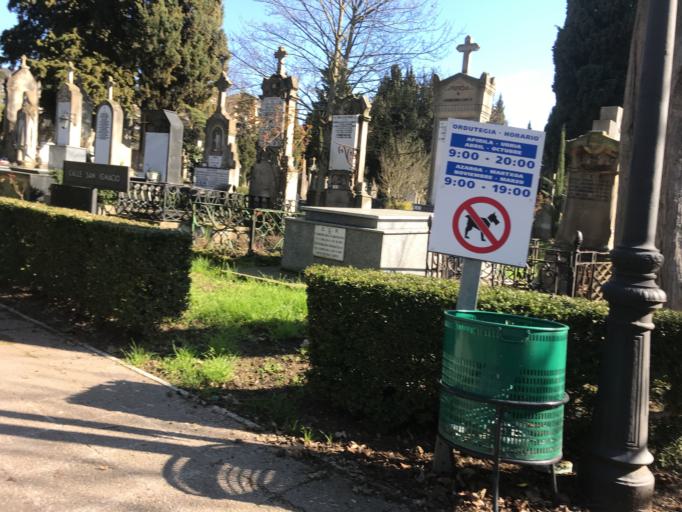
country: ES
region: Basque Country
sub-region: Provincia de Alava
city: Gasteiz / Vitoria
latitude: 42.8582
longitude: -2.6735
